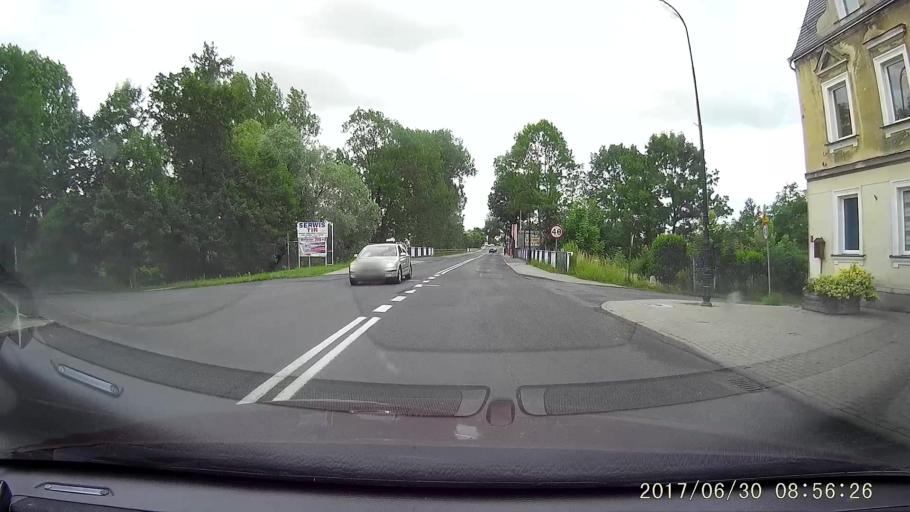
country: PL
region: Lower Silesian Voivodeship
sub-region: Powiat zgorzelecki
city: Zgorzelec
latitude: 51.1344
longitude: 15.0149
